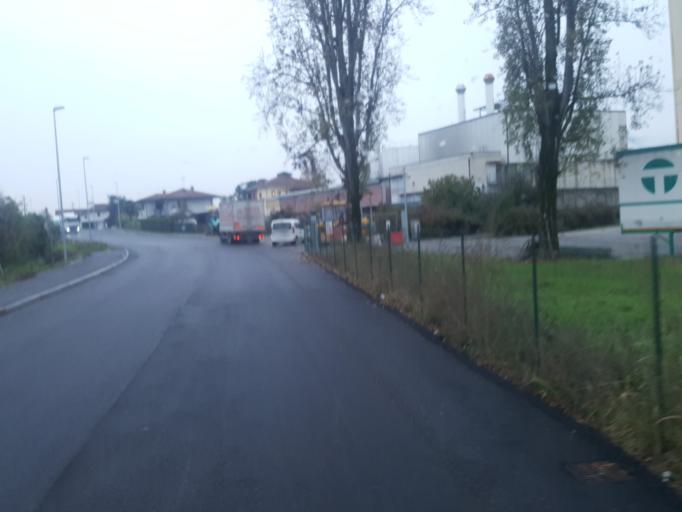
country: IT
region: Piedmont
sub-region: Provincia di Cuneo
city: Saluzzo
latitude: 44.6409
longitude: 7.5073
